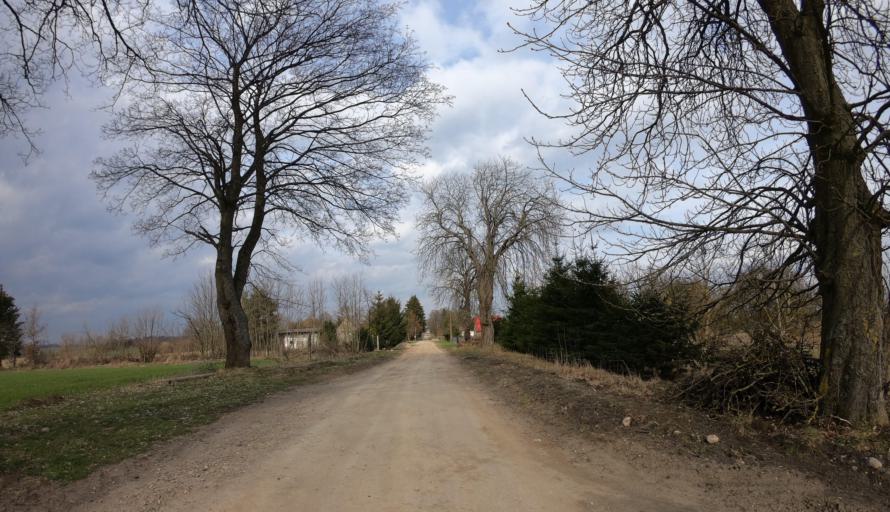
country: PL
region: West Pomeranian Voivodeship
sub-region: Powiat swidwinski
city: Rabino
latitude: 53.8748
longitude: 15.8817
